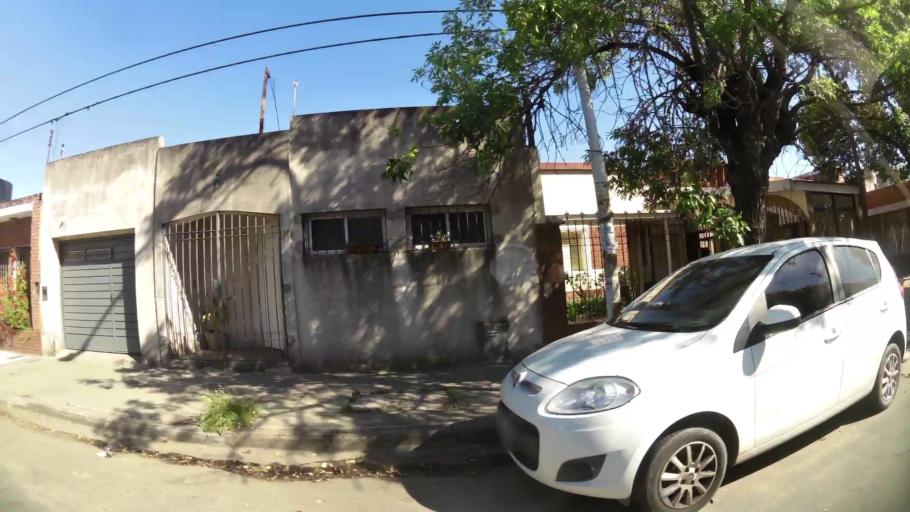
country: AR
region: Cordoba
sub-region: Departamento de Capital
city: Cordoba
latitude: -31.4349
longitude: -64.1534
